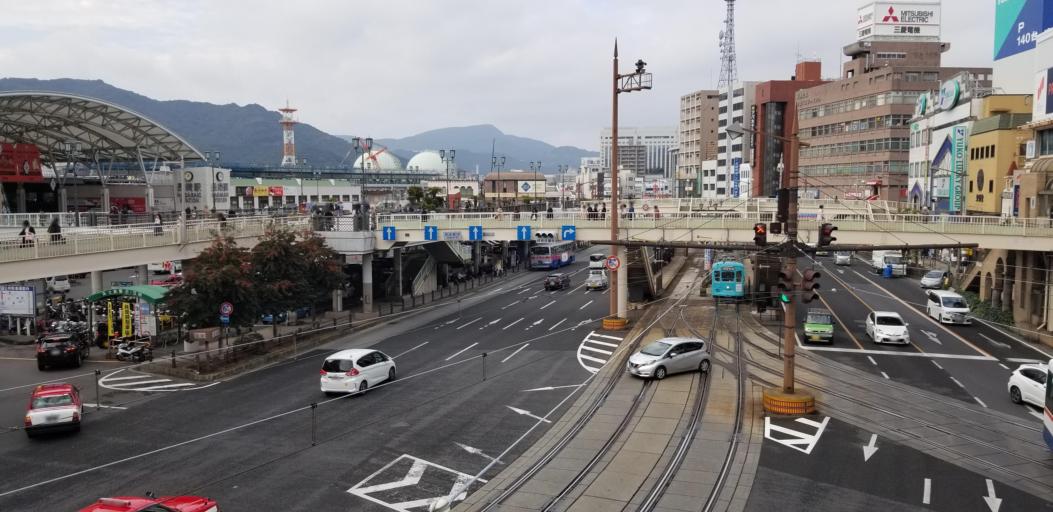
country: JP
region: Nagasaki
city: Nagasaki-shi
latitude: 32.7519
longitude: 129.8722
